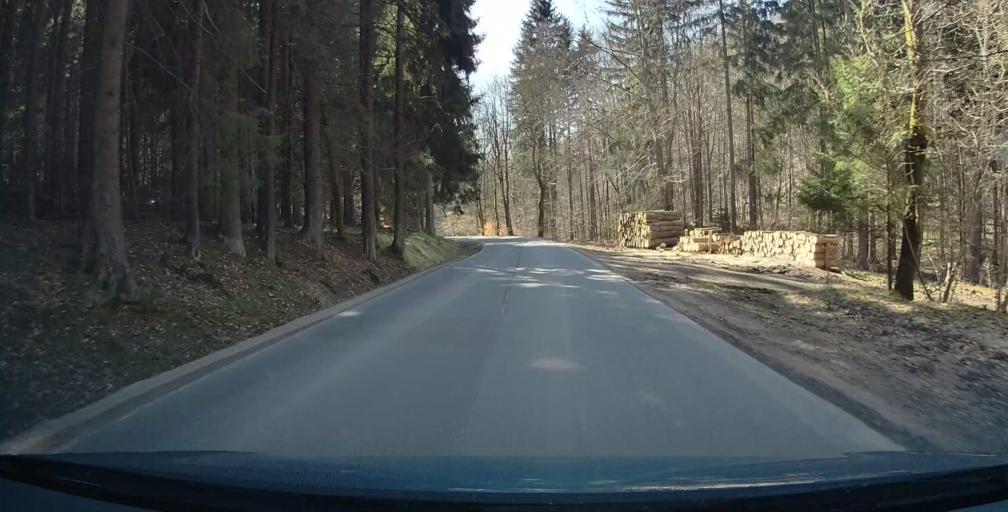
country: PL
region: Lower Silesian Voivodeship
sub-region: Powiat klodzki
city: Lewin Klodzki
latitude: 50.4509
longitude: 16.2914
